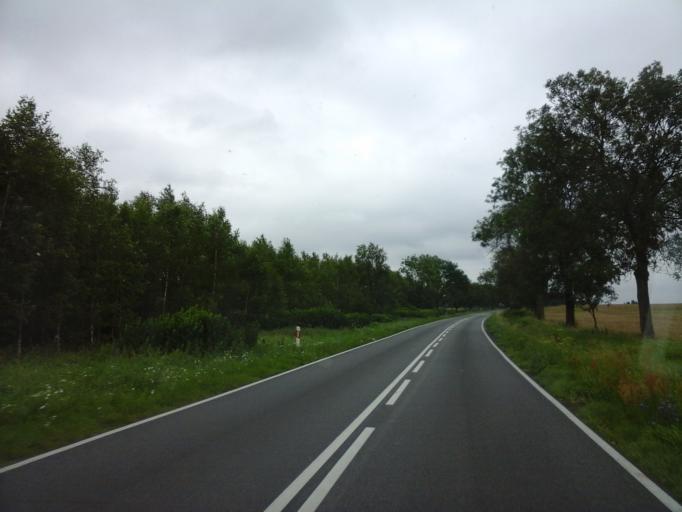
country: PL
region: West Pomeranian Voivodeship
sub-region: Powiat choszczenski
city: Pelczyce
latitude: 53.0614
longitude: 15.3018
